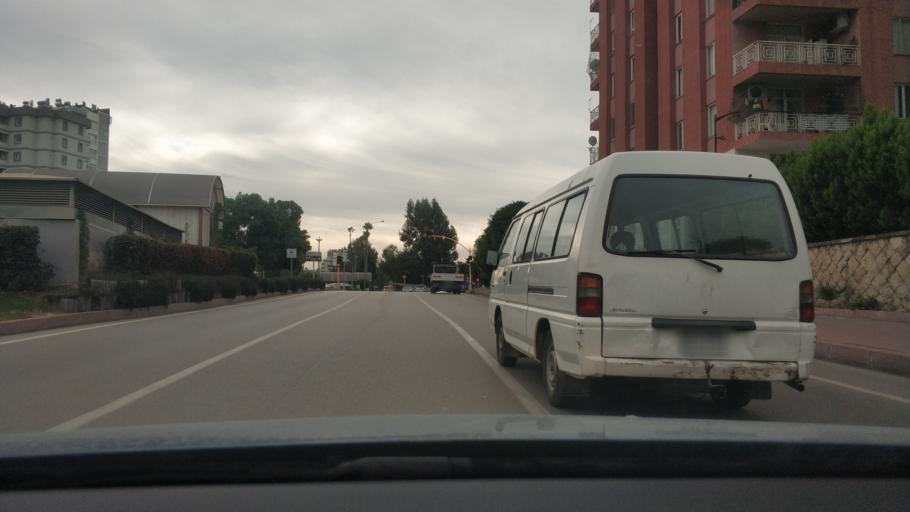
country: TR
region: Adana
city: Adana
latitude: 37.0026
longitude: 35.3128
